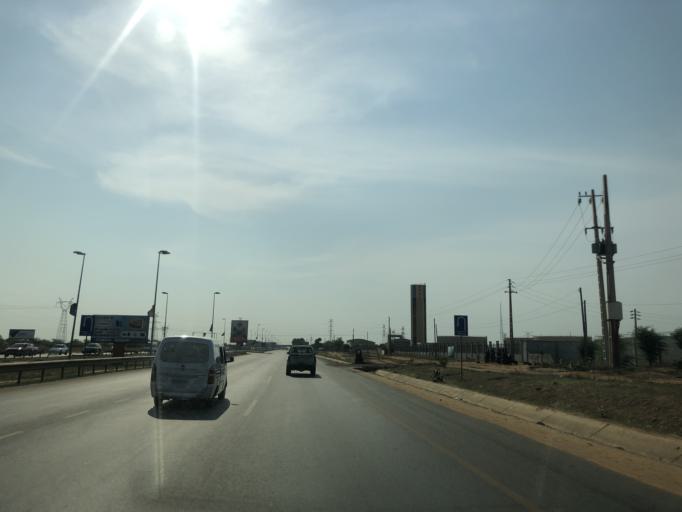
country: AO
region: Luanda
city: Luanda
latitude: -8.9732
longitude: 13.2643
